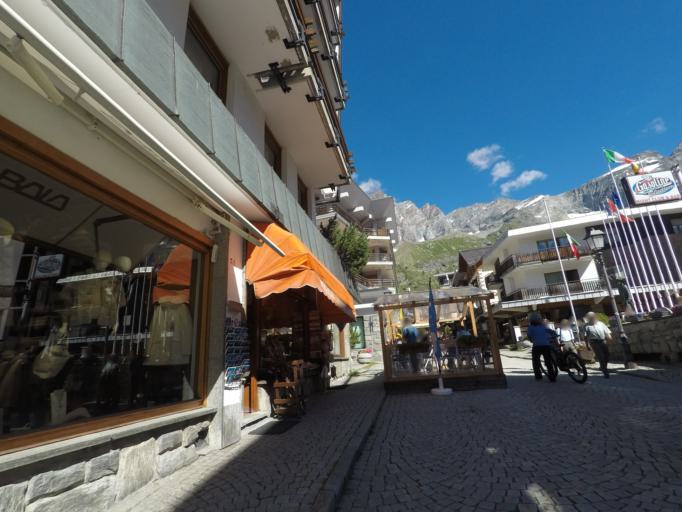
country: IT
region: Aosta Valley
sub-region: Valle d'Aosta
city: Paquier
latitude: 45.9360
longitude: 7.6302
